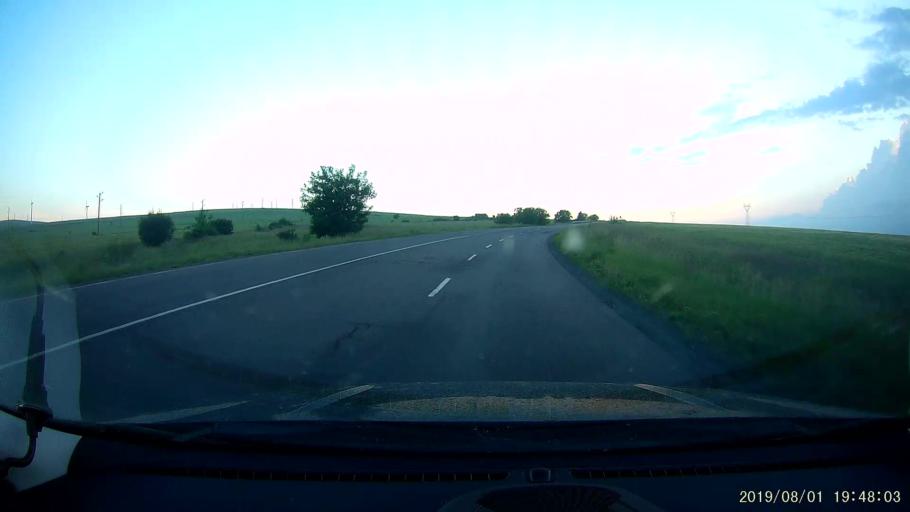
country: BG
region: Burgas
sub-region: Obshtina Karnobat
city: Karnobat
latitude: 42.6421
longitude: 26.9566
